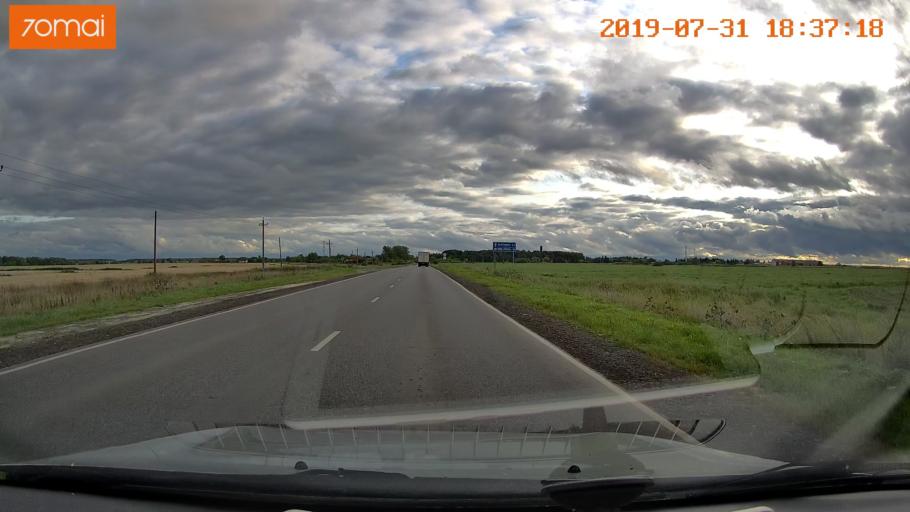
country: RU
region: Moskovskaya
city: Voskresensk
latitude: 55.2801
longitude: 38.6625
